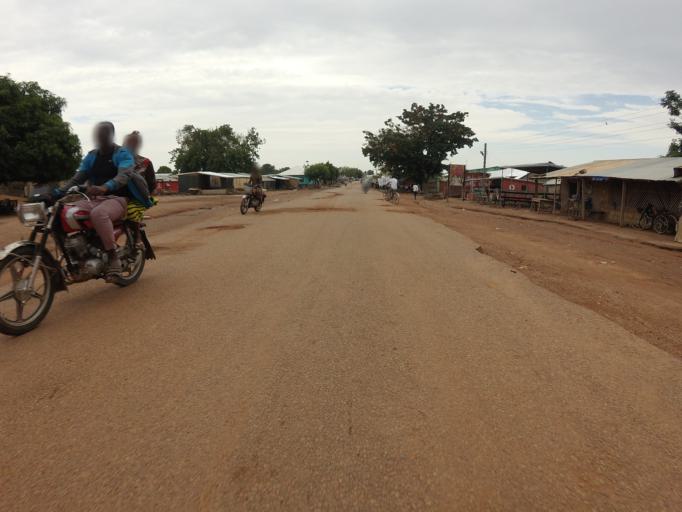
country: GH
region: Upper East
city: Bawku
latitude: 10.9378
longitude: -0.4887
